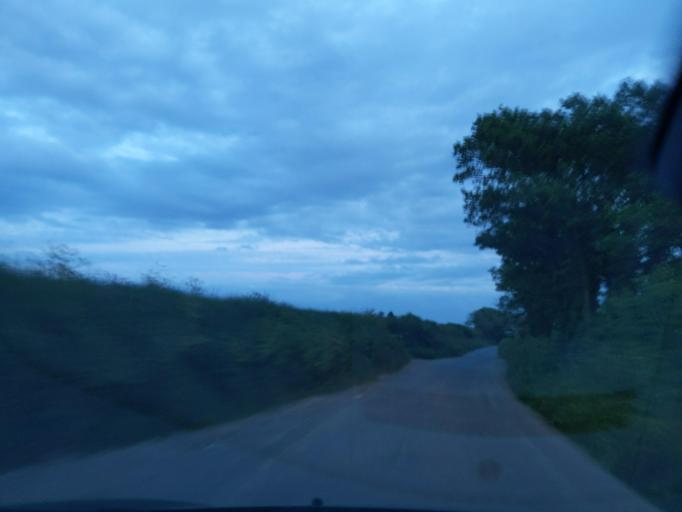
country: GB
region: England
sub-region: Cornwall
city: Wadebridge
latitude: 50.5805
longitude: -4.8336
